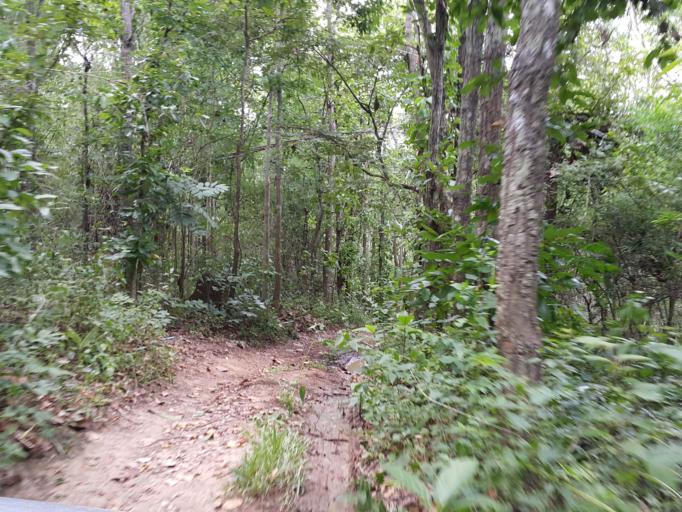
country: TH
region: Chiang Mai
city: Hang Dong
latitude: 18.7643
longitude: 98.9052
